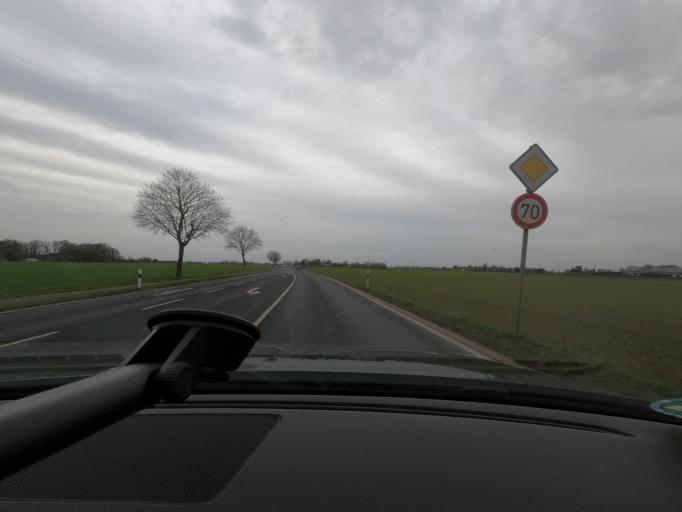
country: DE
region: North Rhine-Westphalia
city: Tonisvorst
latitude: 51.3333
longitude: 6.5137
